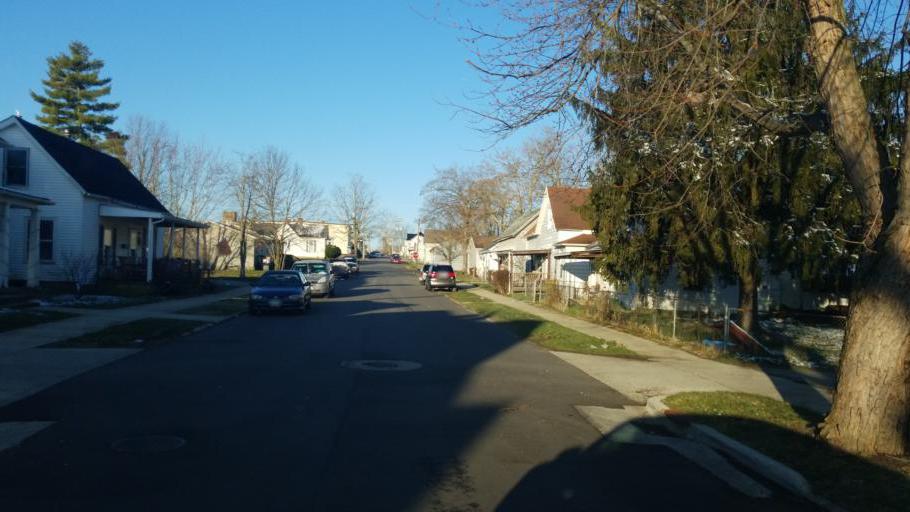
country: US
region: Ohio
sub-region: Highland County
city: Greenfield
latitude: 39.3534
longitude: -83.3803
